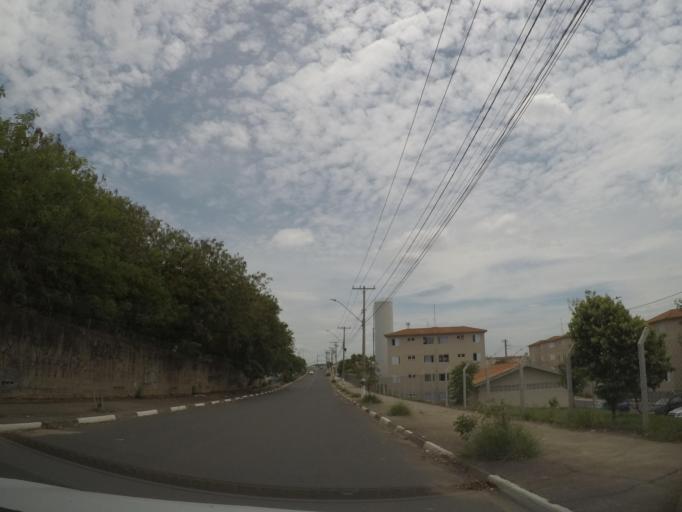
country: BR
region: Sao Paulo
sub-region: Hortolandia
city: Hortolandia
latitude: -22.8474
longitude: -47.2005
